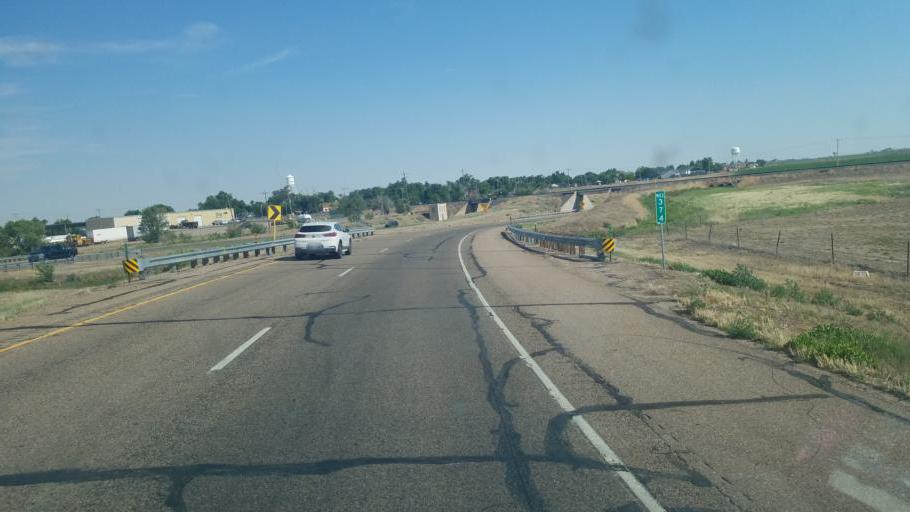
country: US
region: Colorado
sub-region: Otero County
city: Rocky Ford
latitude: 38.0198
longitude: -103.6342
